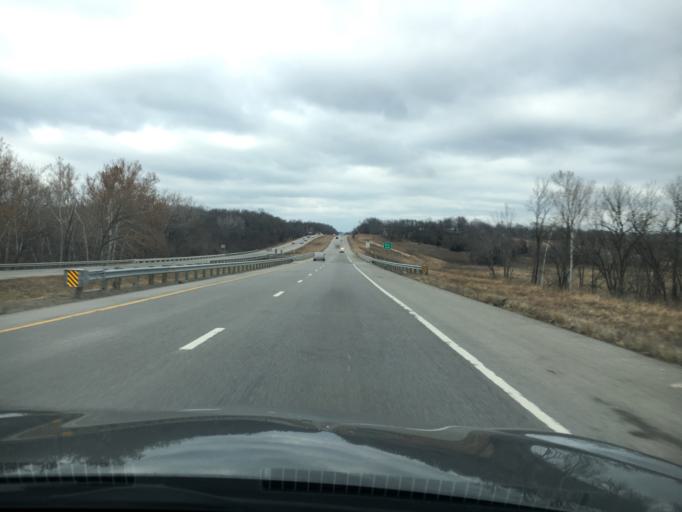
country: US
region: Missouri
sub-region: Cass County
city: Belton
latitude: 38.8108
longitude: -94.6753
